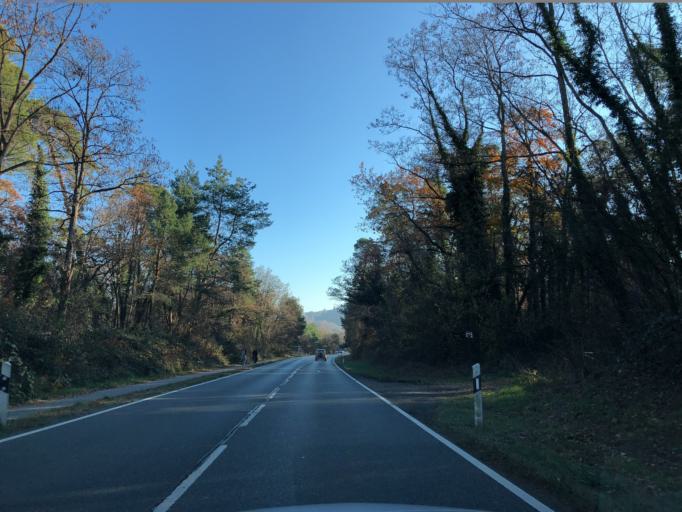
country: DE
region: Hesse
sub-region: Regierungsbezirk Darmstadt
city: Bickenbach
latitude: 49.7649
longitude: 8.6271
